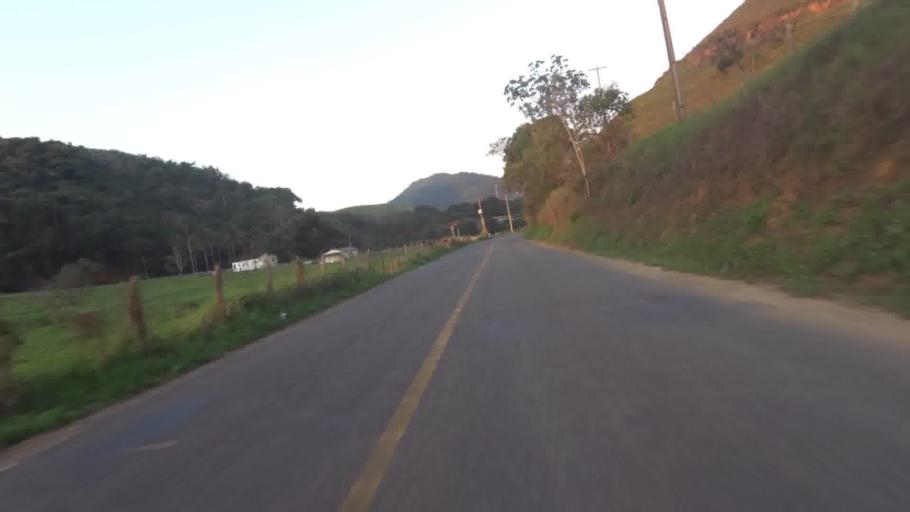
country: BR
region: Espirito Santo
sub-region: Alfredo Chaves
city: Alfredo Chaves
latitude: -20.6505
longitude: -40.6490
